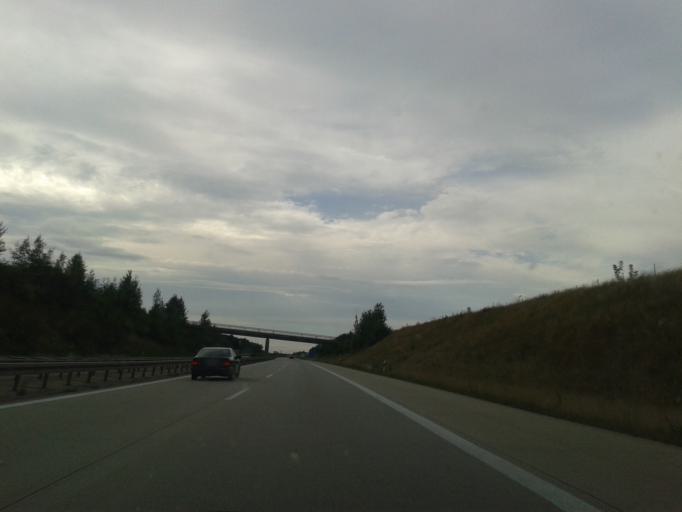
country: DE
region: Saxony
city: Kreischa
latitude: 50.9850
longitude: 13.7830
